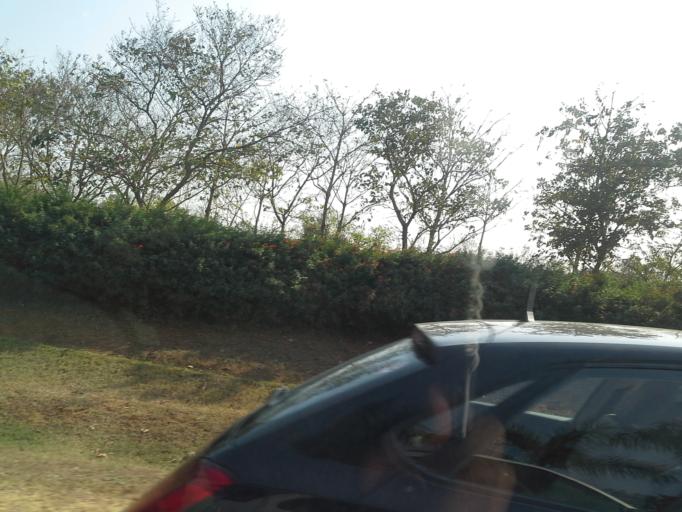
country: IN
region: Telangana
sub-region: Rangareddi
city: Balapur
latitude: 17.2451
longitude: 78.4011
